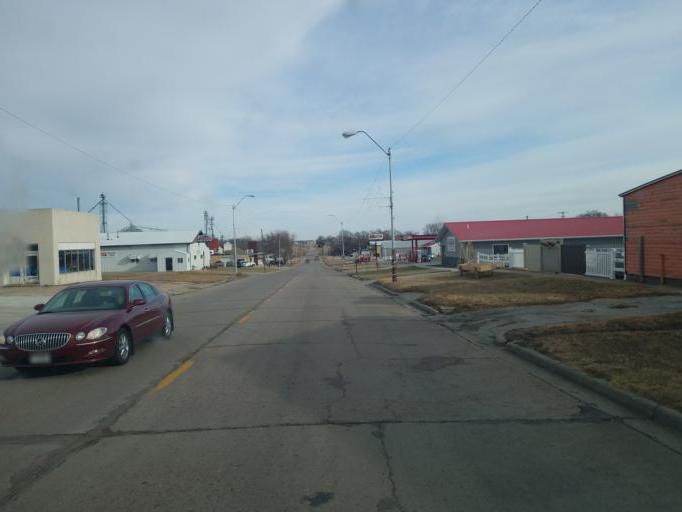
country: US
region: Nebraska
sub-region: Knox County
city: Creighton
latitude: 42.4667
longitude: -97.9043
